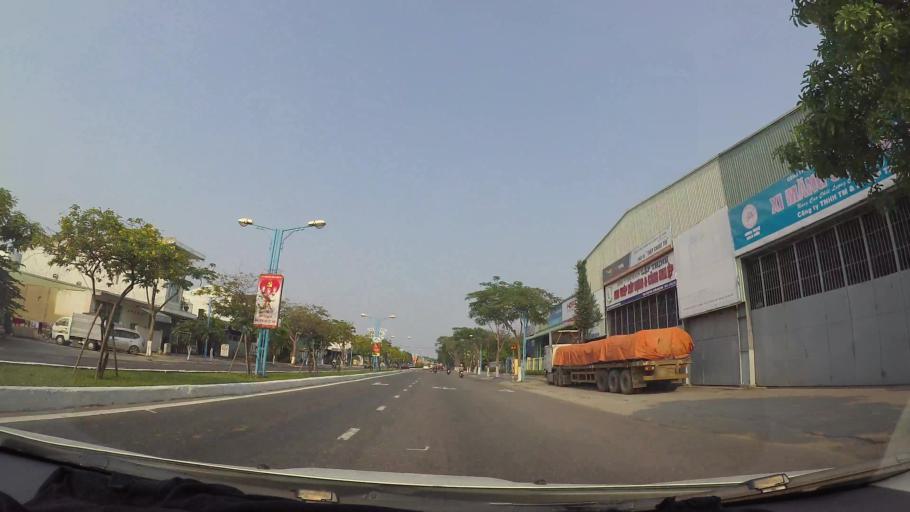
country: VN
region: Da Nang
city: Cam Le
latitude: 16.0216
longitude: 108.1995
